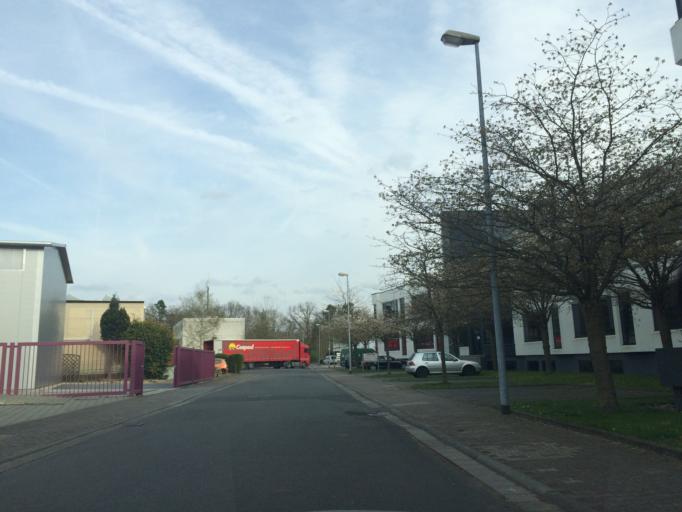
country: DE
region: Hesse
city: Langen
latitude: 50.0196
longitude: 8.6581
